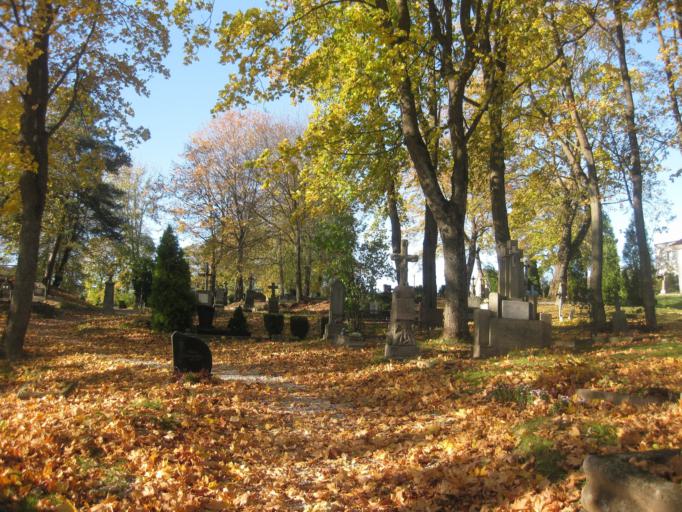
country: LT
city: Vilkija
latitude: 55.0401
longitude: 23.5890
